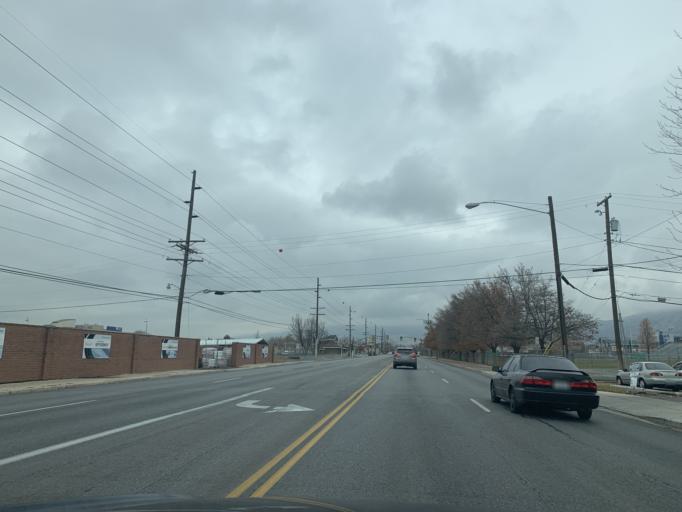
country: US
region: Utah
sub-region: Utah County
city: Provo
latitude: 40.2469
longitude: -111.6620
